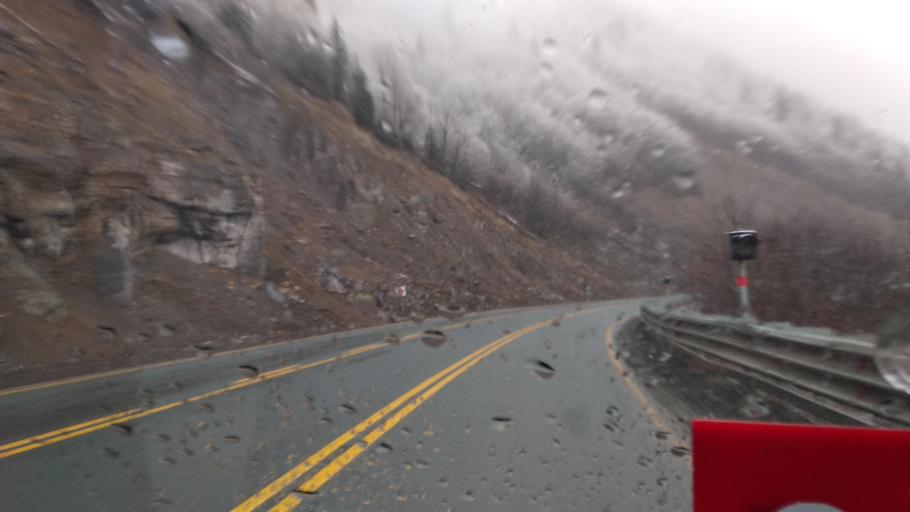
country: TR
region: Trabzon
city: Macka
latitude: 40.7013
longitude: 39.4855
